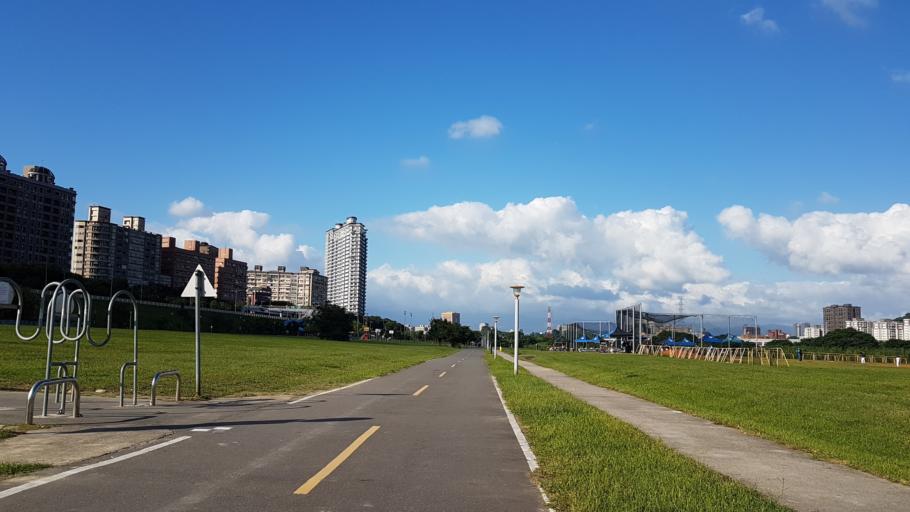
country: TW
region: Taipei
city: Taipei
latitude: 24.9940
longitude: 121.5291
